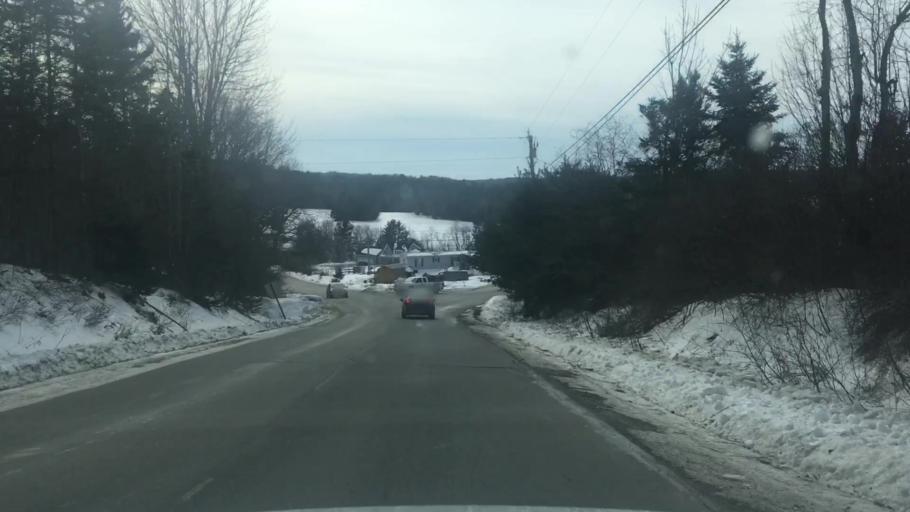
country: US
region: Maine
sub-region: Hancock County
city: Orland
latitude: 44.5977
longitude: -68.7234
